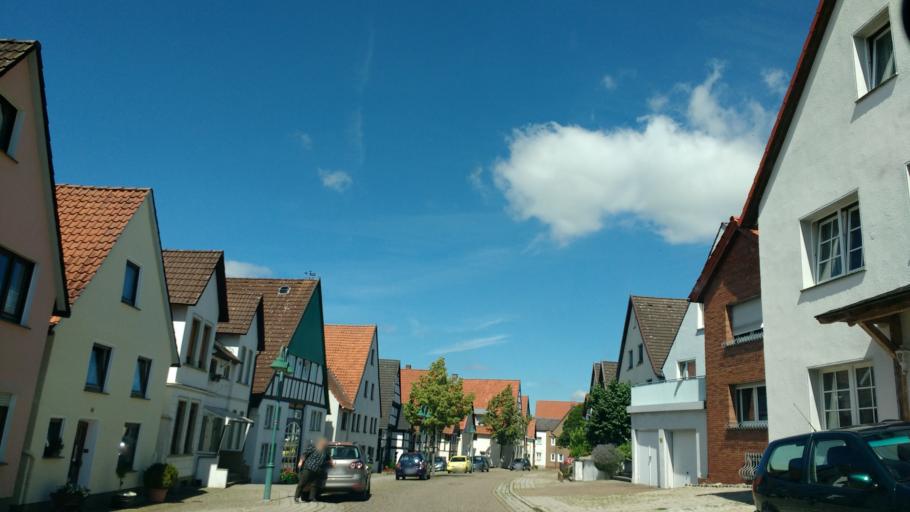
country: DE
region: North Rhine-Westphalia
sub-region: Regierungsbezirk Detmold
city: Barntrup
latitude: 51.9901
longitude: 9.1093
